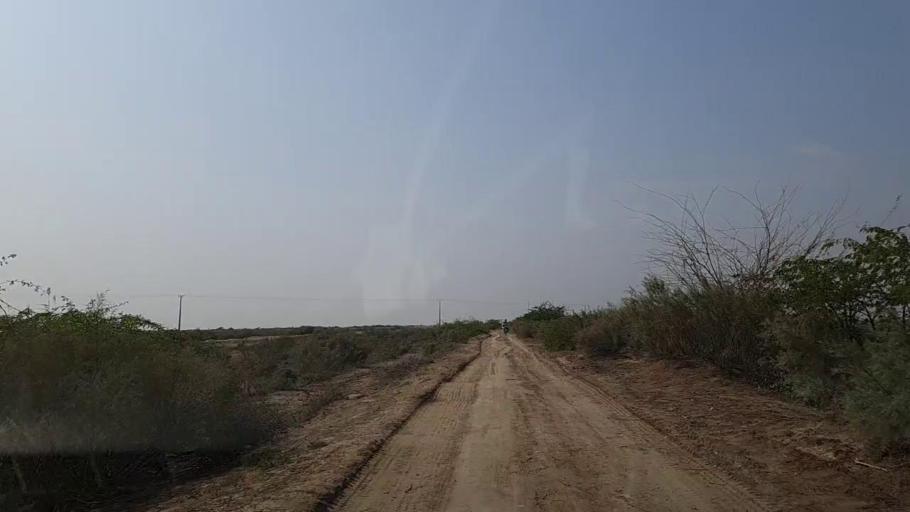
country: PK
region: Sindh
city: Gharo
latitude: 24.6735
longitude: 67.7042
